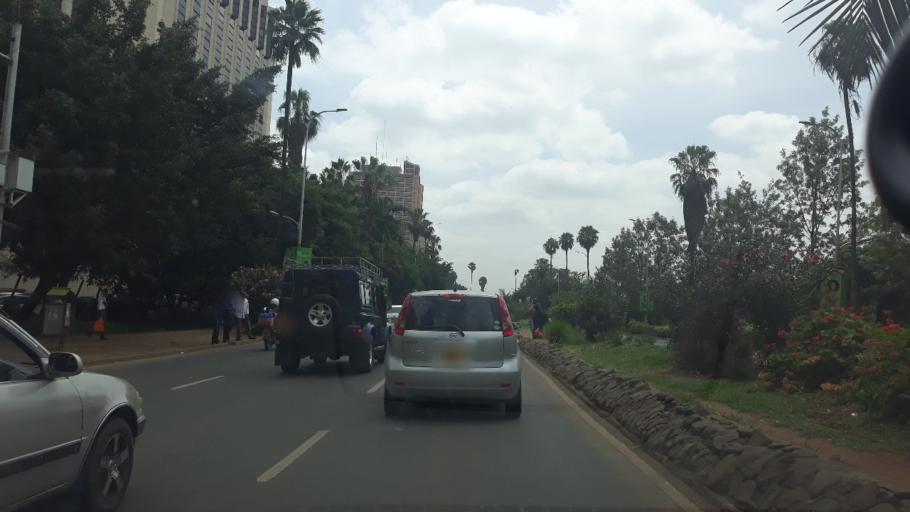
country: KE
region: Nairobi Area
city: Nairobi
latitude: -1.2836
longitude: 36.8159
